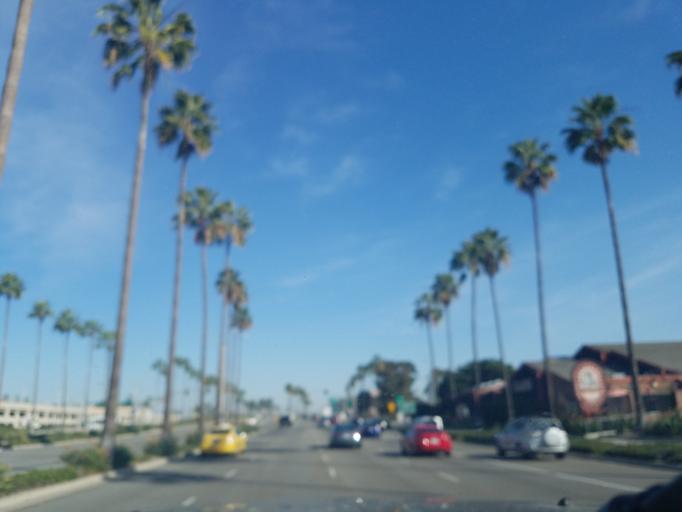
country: US
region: California
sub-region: Orange County
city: Irvine
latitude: 33.6793
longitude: -117.8593
